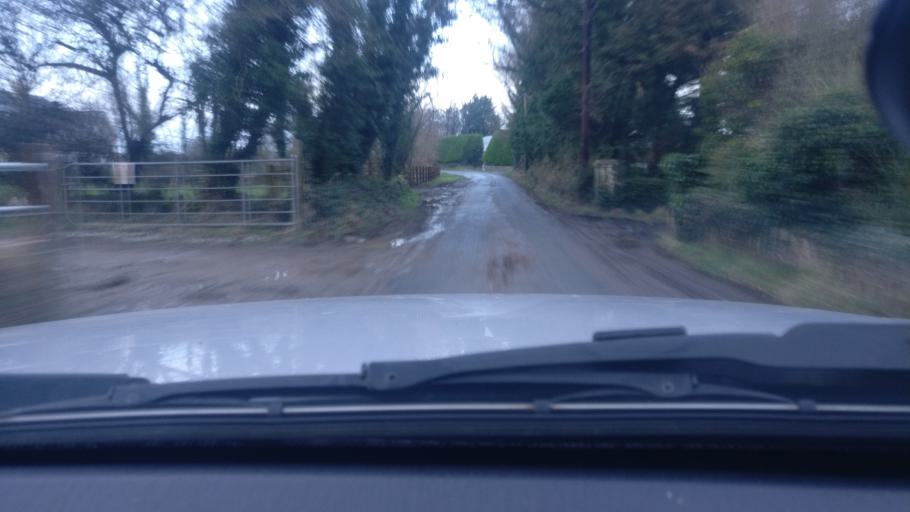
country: IE
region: Connaught
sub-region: County Galway
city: Loughrea
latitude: 53.1756
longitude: -8.5872
